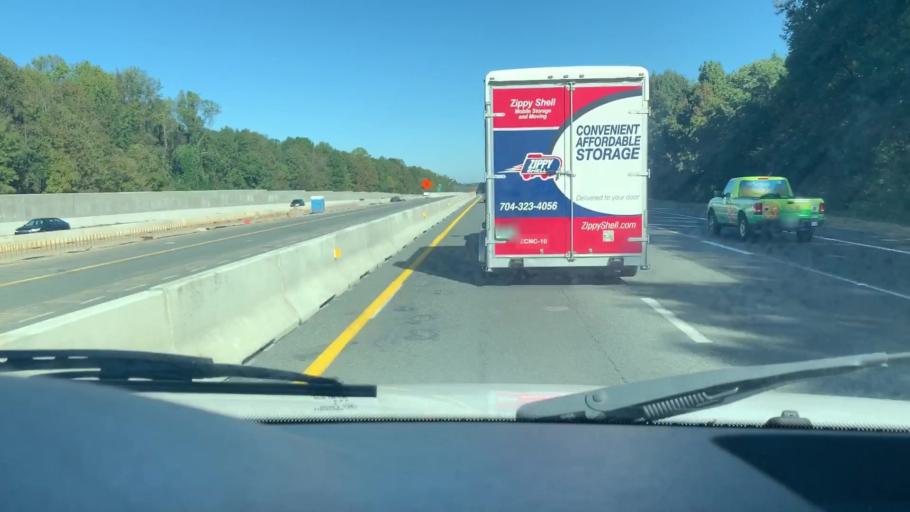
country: US
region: North Carolina
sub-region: Mecklenburg County
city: Huntersville
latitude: 35.3241
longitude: -80.8478
